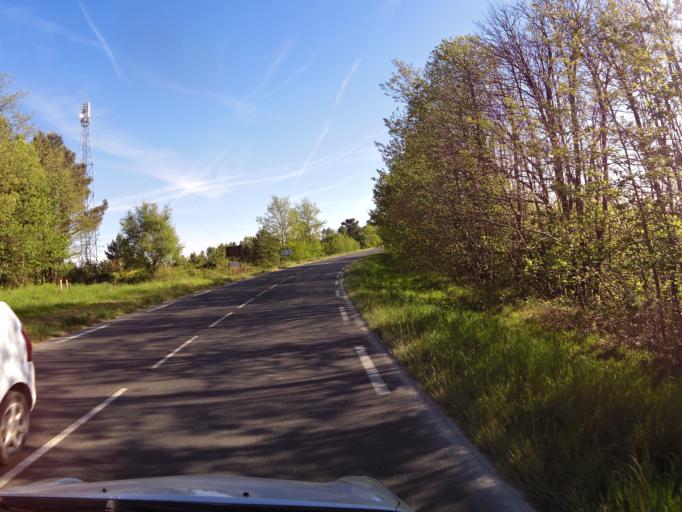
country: FR
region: Aquitaine
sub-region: Departement de la Dordogne
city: Sarlat-la-Caneda
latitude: 44.9525
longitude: 1.2242
